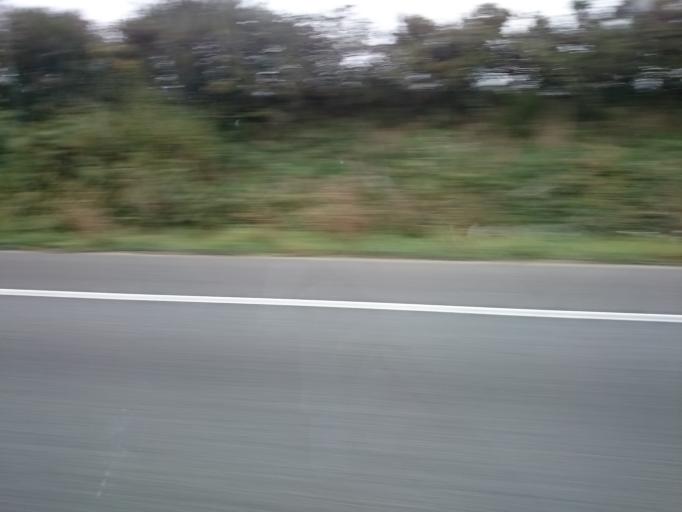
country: FR
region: Brittany
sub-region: Departement du Morbihan
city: Ploeren
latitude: 47.6613
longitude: -2.8342
